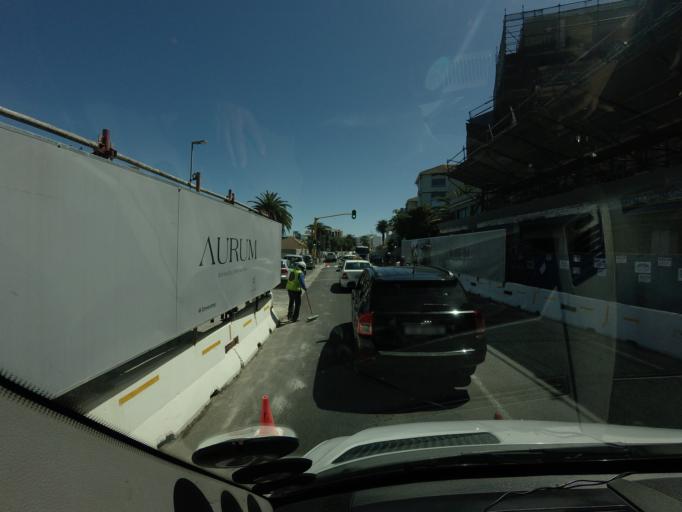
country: ZA
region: Western Cape
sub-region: City of Cape Town
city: Cape Town
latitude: -33.9272
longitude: 18.3782
